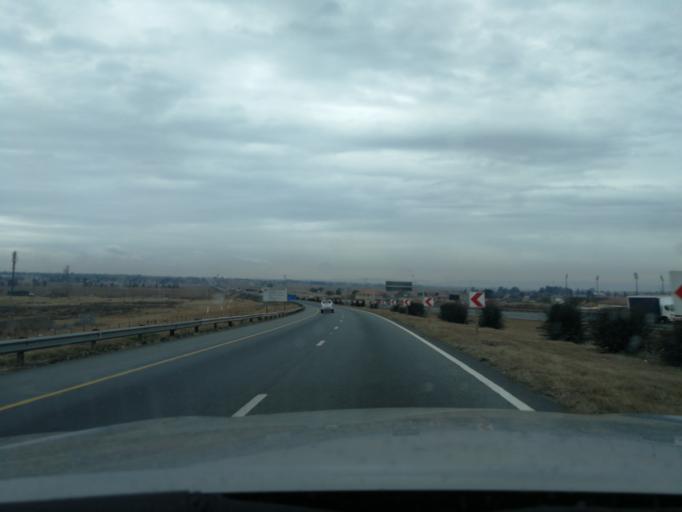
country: ZA
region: Gauteng
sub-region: Ekurhuleni Metropolitan Municipality
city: Germiston
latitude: -26.2941
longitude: 28.1566
